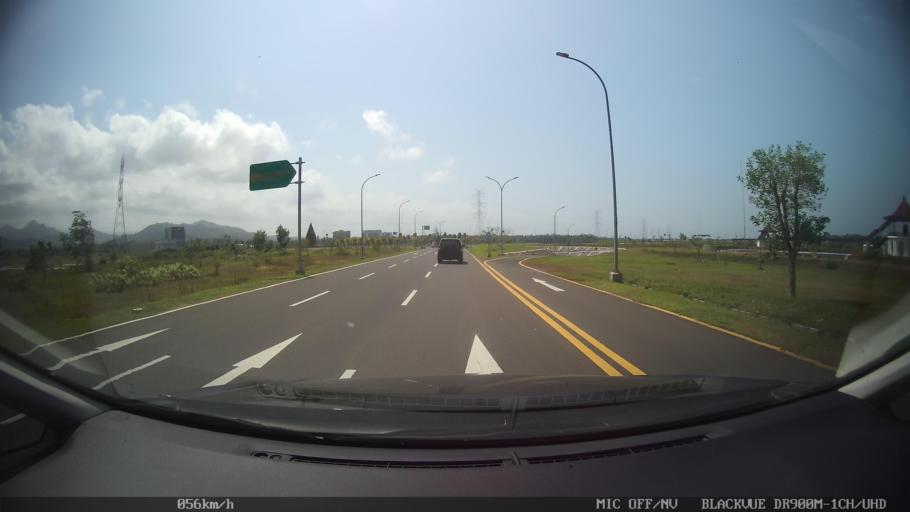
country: ID
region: Daerah Istimewa Yogyakarta
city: Srandakan
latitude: -7.8918
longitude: 110.0599
